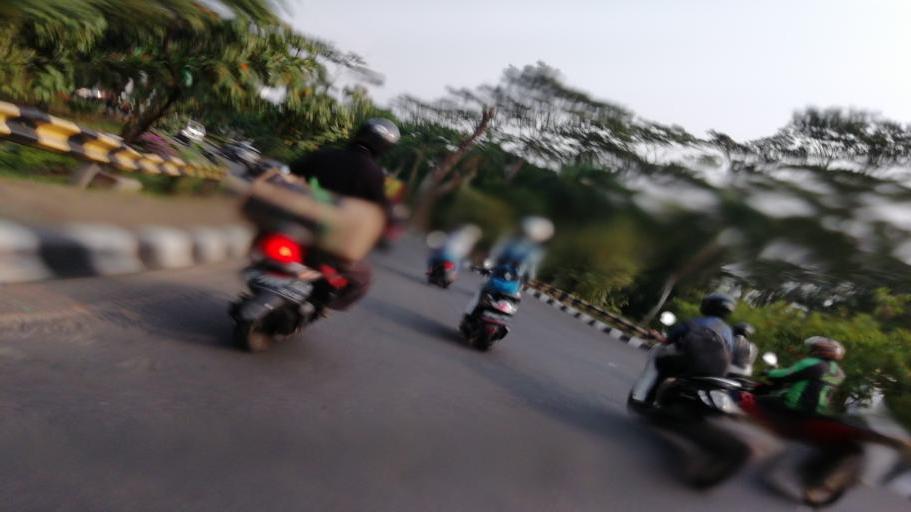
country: ID
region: West Java
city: Depok
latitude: -6.3564
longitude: 106.8304
